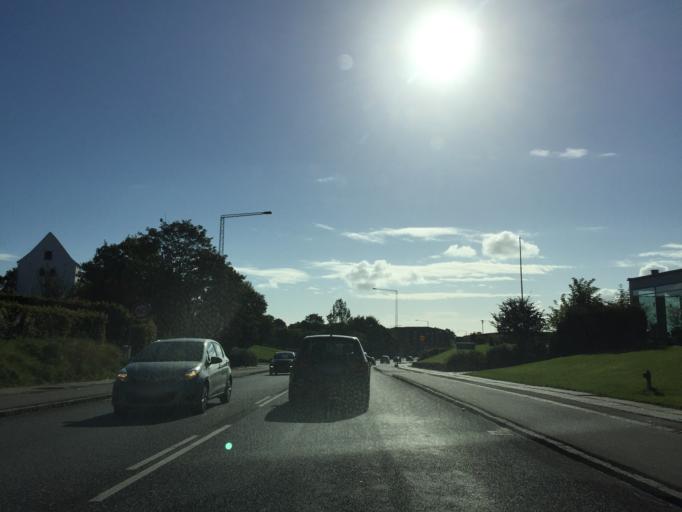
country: DK
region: Central Jutland
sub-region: Arhus Kommune
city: Arhus
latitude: 56.1699
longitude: 10.1593
